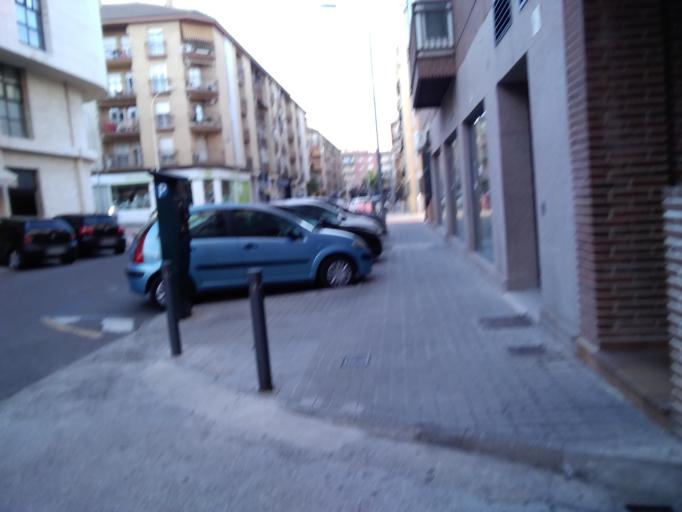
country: ES
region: Castille-La Mancha
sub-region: Province of Toledo
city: Toledo
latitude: 39.8686
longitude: -4.0326
